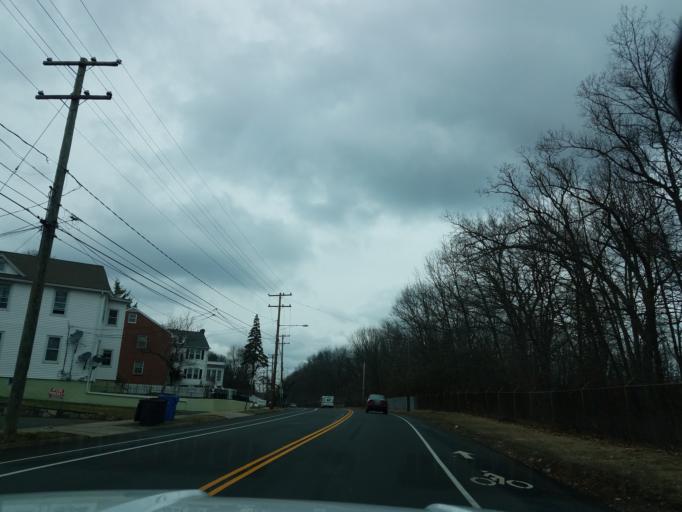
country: US
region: Connecticut
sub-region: Hartford County
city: New Britain
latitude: 41.6786
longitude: -72.8043
